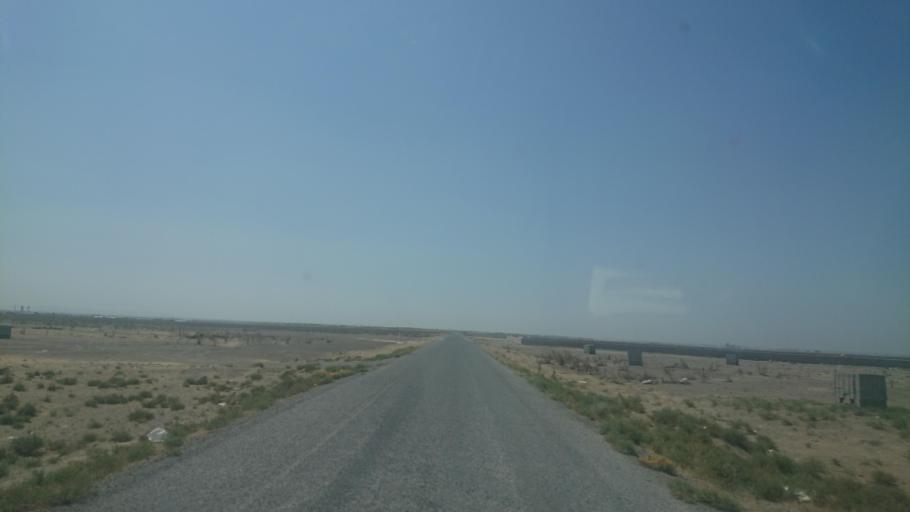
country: TR
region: Aksaray
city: Yesilova
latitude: 38.3271
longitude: 33.7472
